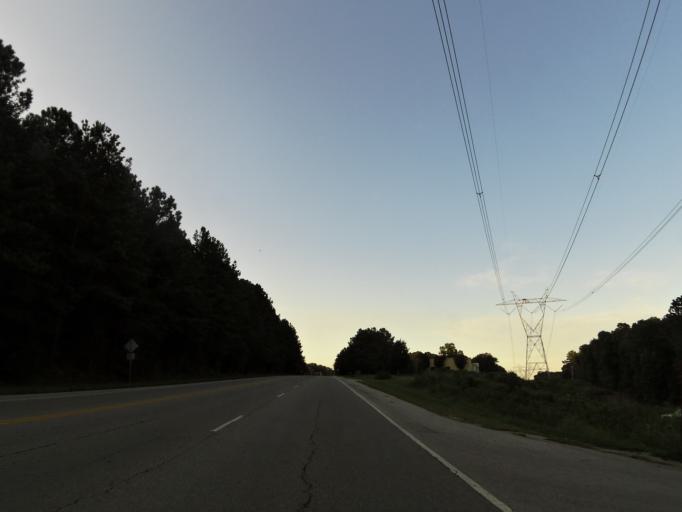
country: US
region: Tennessee
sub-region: Roane County
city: Midtown
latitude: 35.8274
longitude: -84.5462
